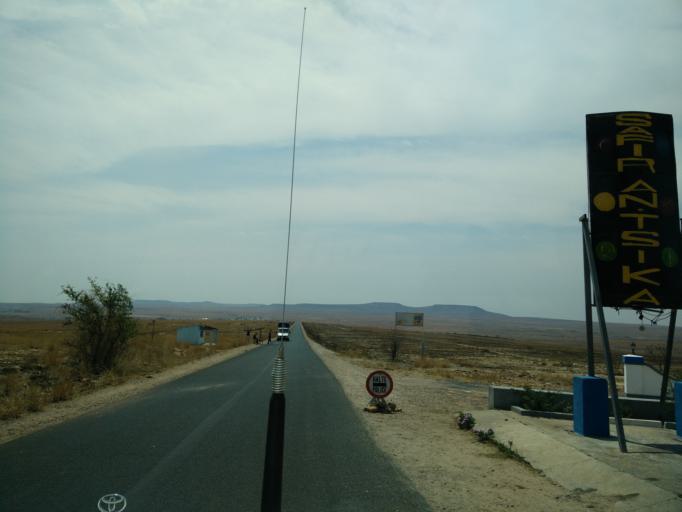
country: MG
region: Ihorombe
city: Ranohira
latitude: -22.7793
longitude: 45.0803
